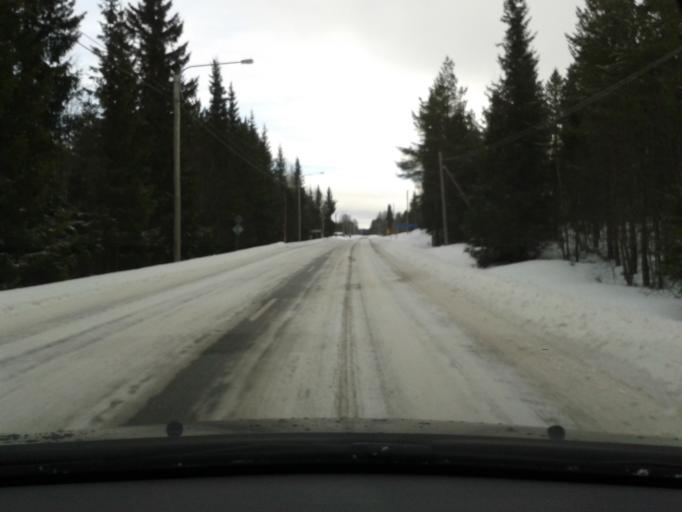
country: SE
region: Vaesterbotten
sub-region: Vilhelmina Kommun
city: Sjoberg
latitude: 64.6513
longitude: 16.3298
